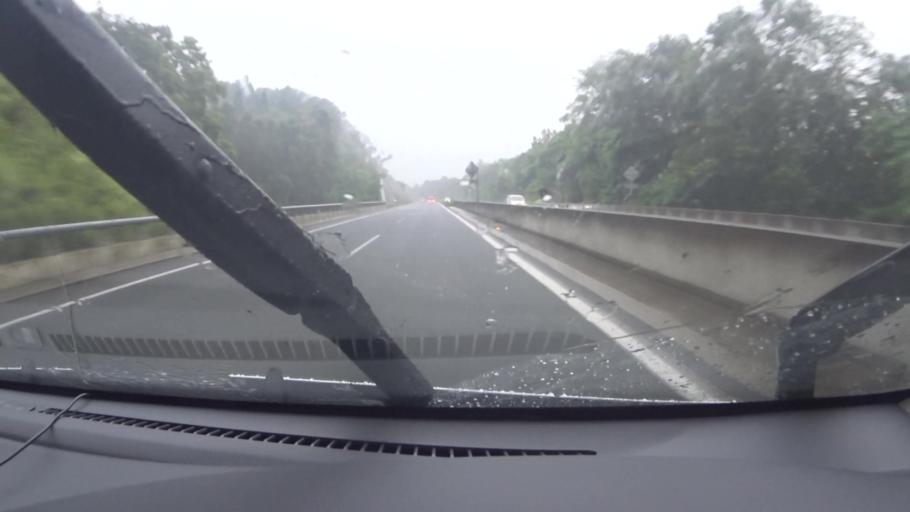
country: JP
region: Kyoto
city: Kameoka
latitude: 35.1127
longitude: 135.4807
